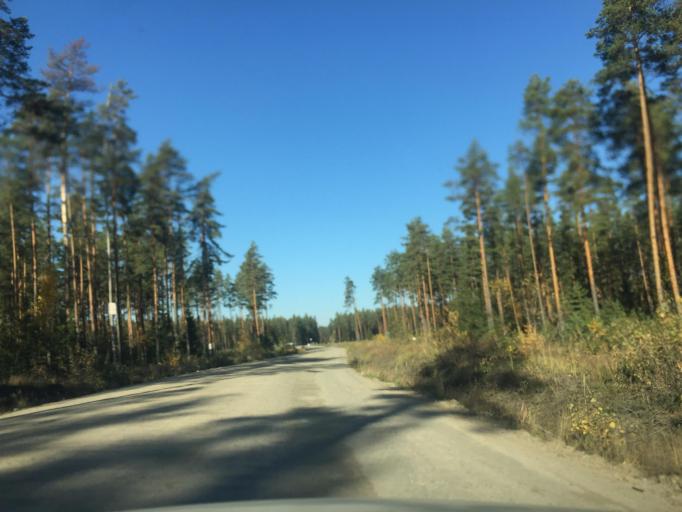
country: RU
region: Republic of Karelia
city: Lakhdenpokh'ya
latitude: 61.3844
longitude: 29.9629
